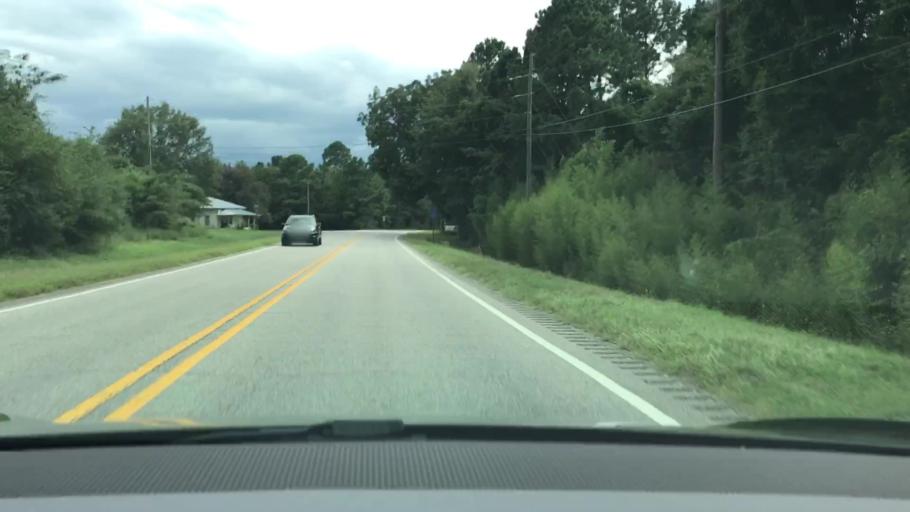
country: US
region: Alabama
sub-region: Coffee County
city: Elba
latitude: 31.5422
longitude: -86.0228
